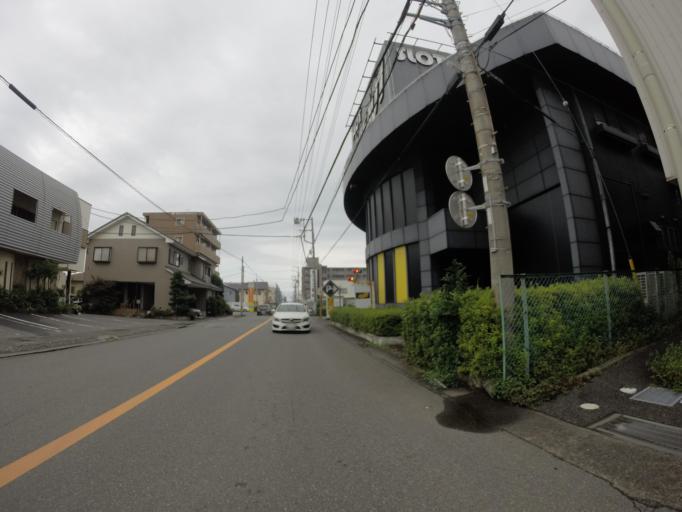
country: JP
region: Shizuoka
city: Numazu
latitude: 35.1155
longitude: 138.8527
